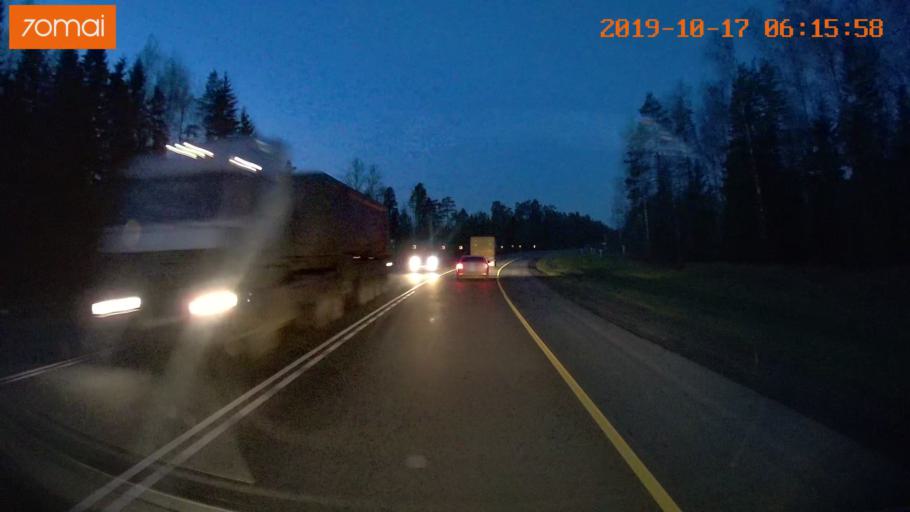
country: RU
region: Ivanovo
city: Lezhnevo
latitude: 56.8663
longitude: 40.9372
